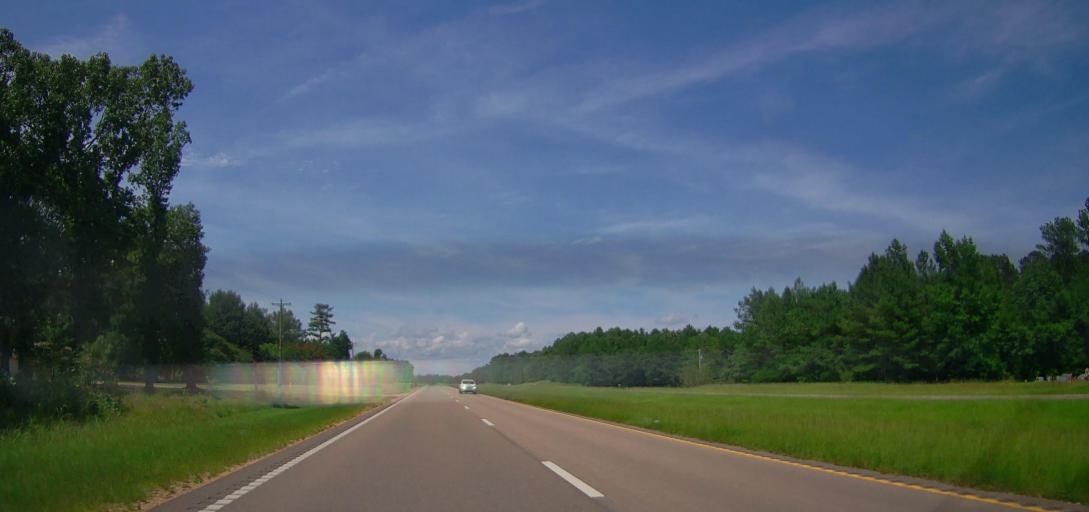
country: US
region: Mississippi
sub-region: Monroe County
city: Aberdeen
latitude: 33.9206
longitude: -88.5962
